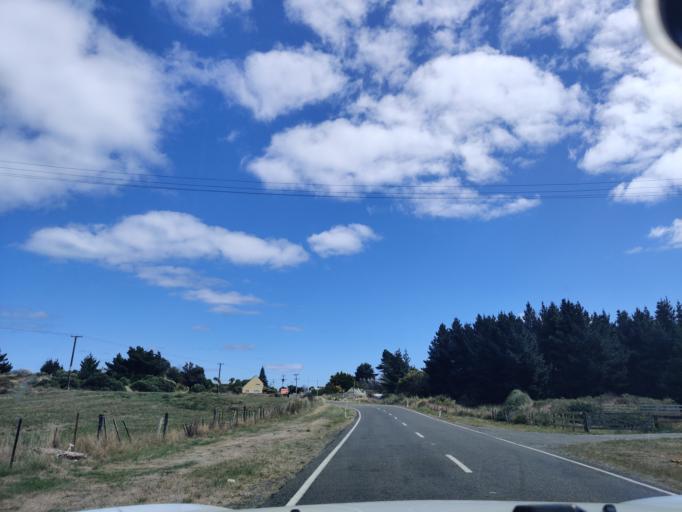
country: NZ
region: Manawatu-Wanganui
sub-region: Horowhenua District
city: Foxton
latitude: -40.3714
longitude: 175.2450
